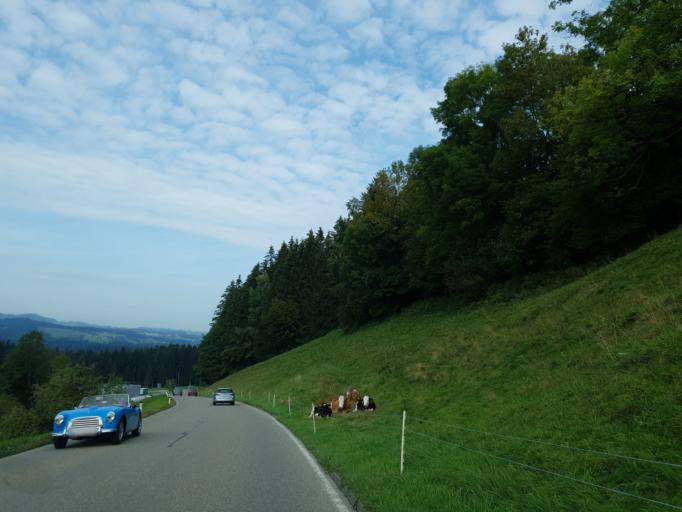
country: AT
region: Vorarlberg
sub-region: Politischer Bezirk Bregenz
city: Doren
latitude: 47.4888
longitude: 9.8523
